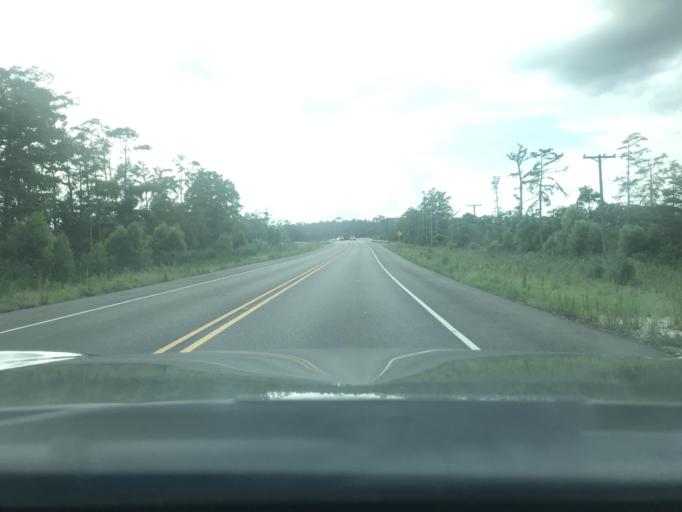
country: US
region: Louisiana
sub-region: Calcasieu Parish
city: Moss Bluff
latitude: 30.3017
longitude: -93.2457
